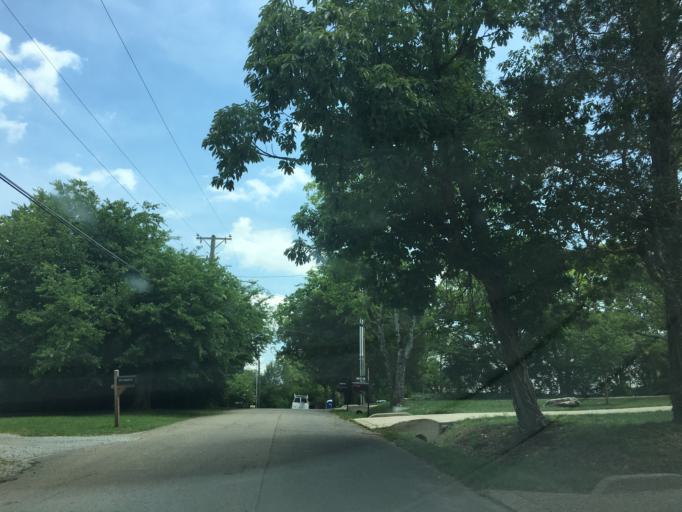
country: US
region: Tennessee
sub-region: Davidson County
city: Oak Hill
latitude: 36.1001
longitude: -86.8147
